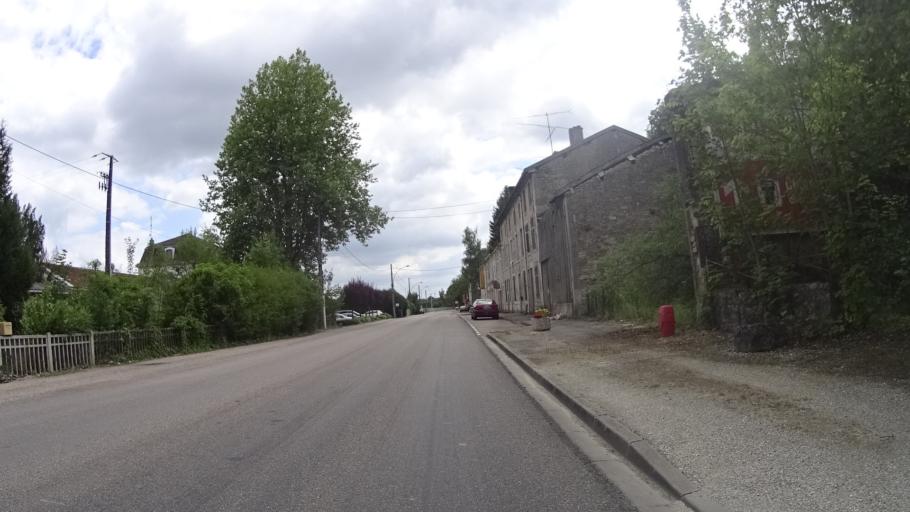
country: FR
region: Lorraine
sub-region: Departement de la Meuse
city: Lerouville
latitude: 48.7971
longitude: 5.5373
